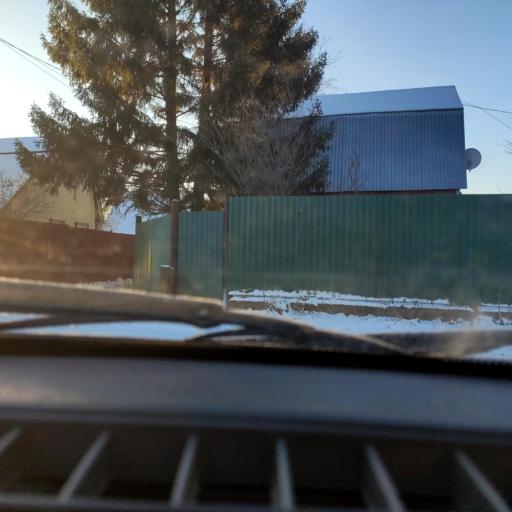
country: RU
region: Bashkortostan
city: Avdon
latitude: 54.6255
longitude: 55.7120
